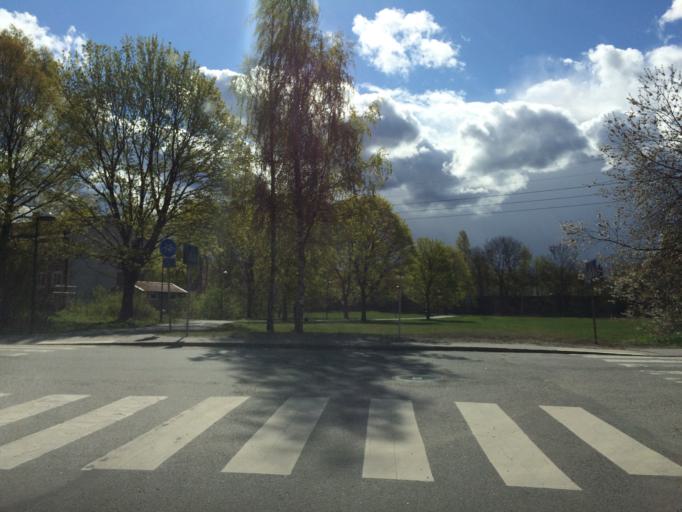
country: SE
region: Stockholm
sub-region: Huddinge Kommun
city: Segeltorp
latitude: 59.2905
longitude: 17.9558
